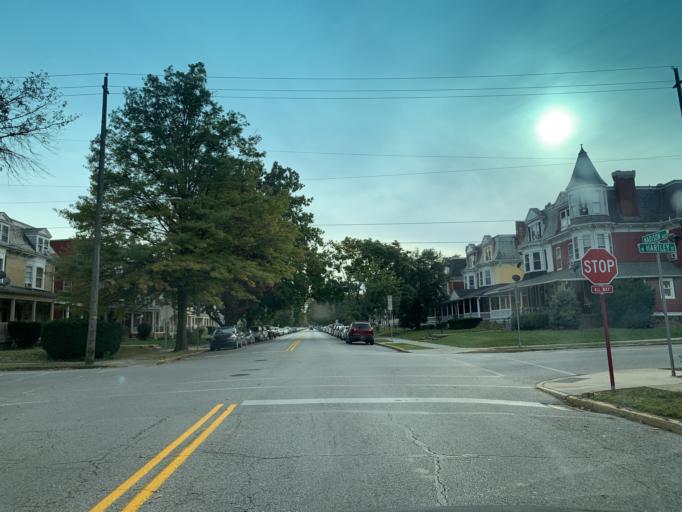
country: US
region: Pennsylvania
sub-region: York County
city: West York
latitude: 39.9642
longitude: -76.7458
